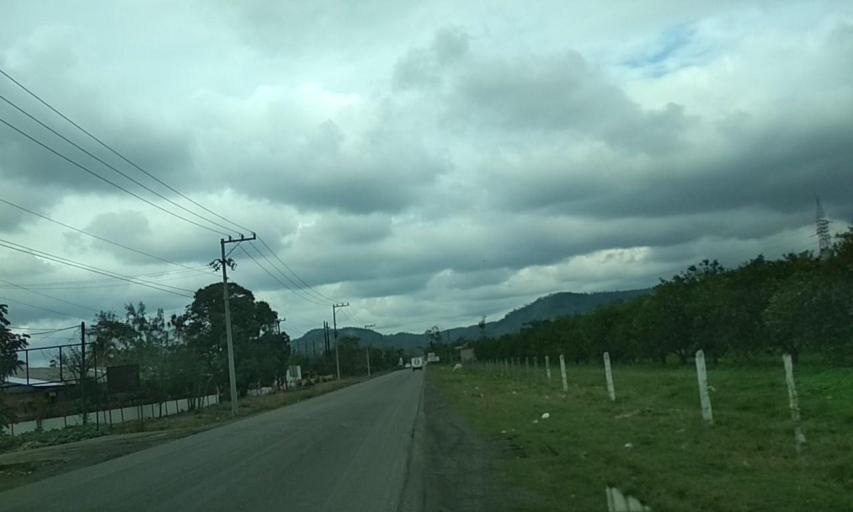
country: MX
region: Veracruz
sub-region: Papantla
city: El Chote
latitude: 20.3928
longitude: -97.3363
